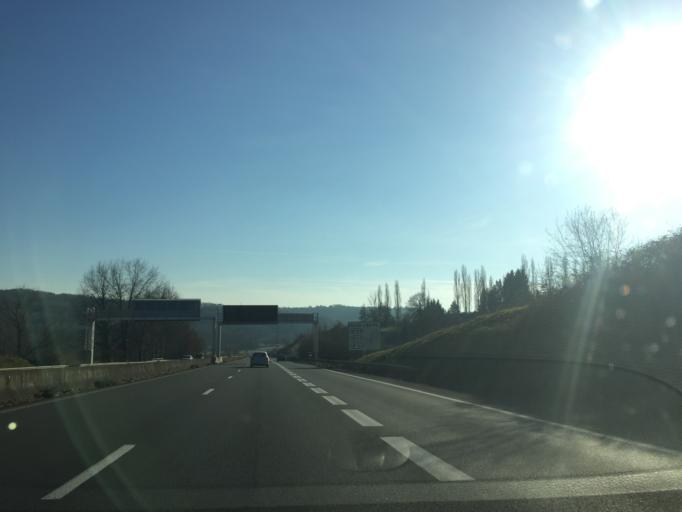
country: FR
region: Limousin
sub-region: Departement de la Correze
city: Donzenac
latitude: 45.2185
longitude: 1.5128
